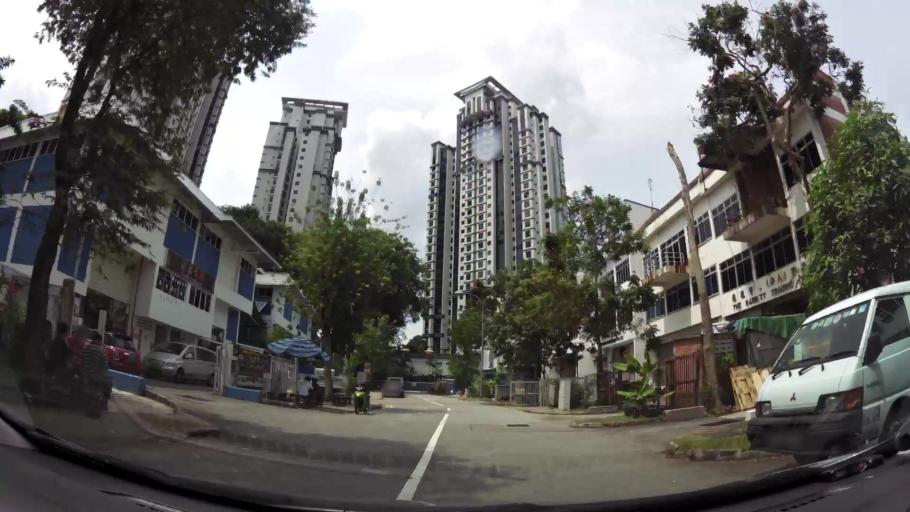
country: SG
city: Singapore
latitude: 1.3527
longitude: 103.7574
